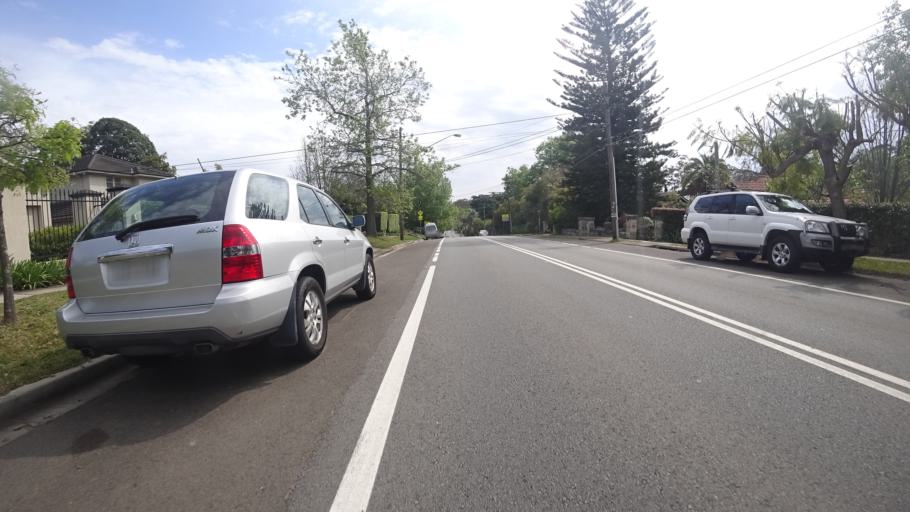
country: AU
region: New South Wales
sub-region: City of Sydney
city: Pymble
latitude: -33.7363
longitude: 151.1372
